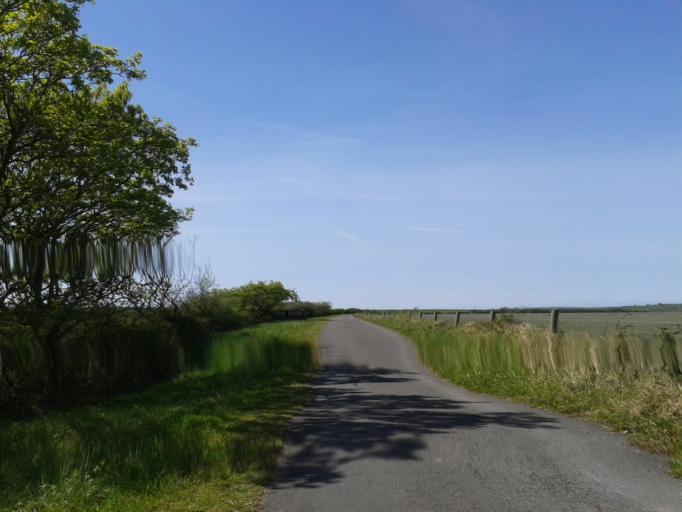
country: GB
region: England
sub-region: Devon
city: Fremington
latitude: 51.0807
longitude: -4.1004
